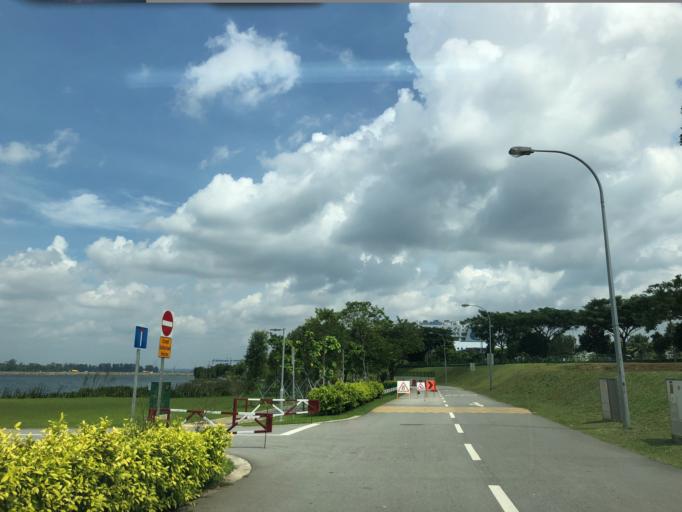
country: MY
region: Johor
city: Kampung Pasir Gudang Baru
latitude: 1.4162
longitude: 103.8608
